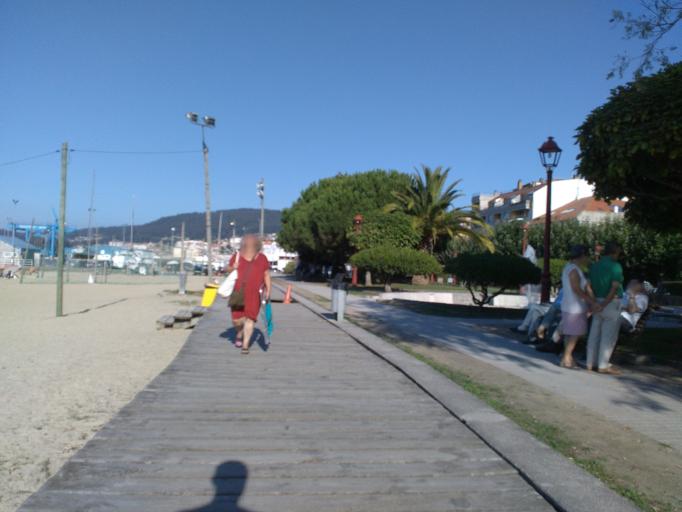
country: ES
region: Galicia
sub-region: Provincia de Pontevedra
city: Bueu
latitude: 42.3269
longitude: -8.7882
